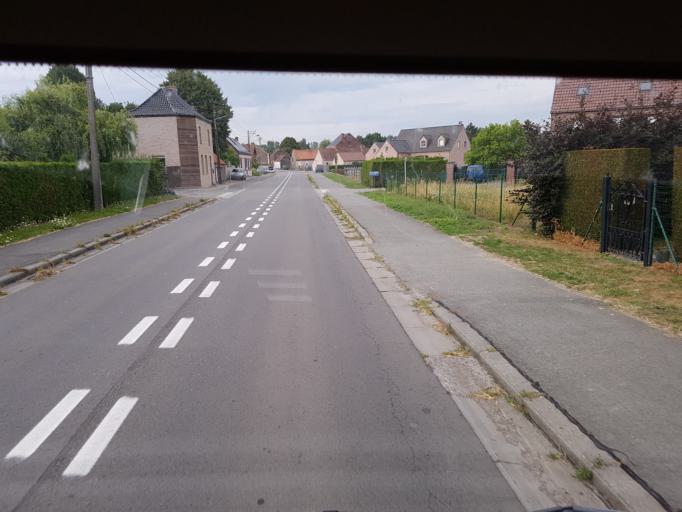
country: FR
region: Nord-Pas-de-Calais
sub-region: Departement du Nord
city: Hergnies
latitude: 50.5182
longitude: 3.5264
